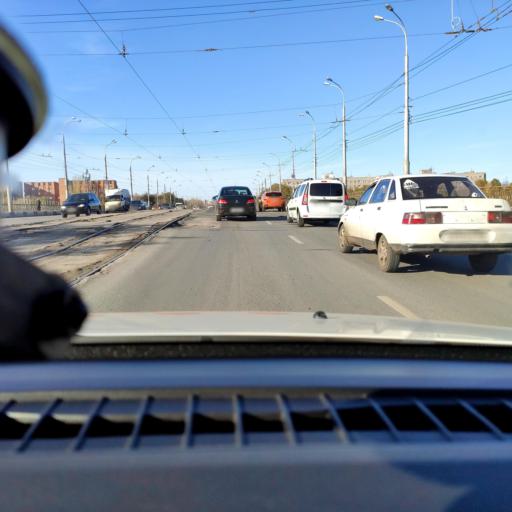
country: RU
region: Samara
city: Samara
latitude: 53.2124
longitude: 50.2713
